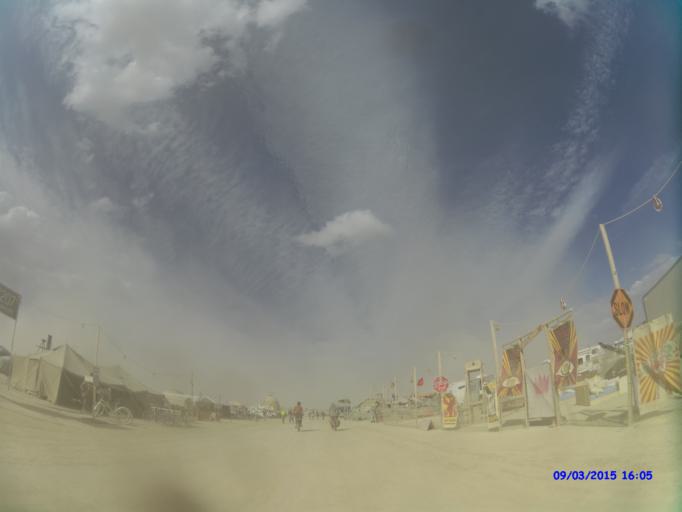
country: US
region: Nevada
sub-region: Pershing County
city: Lovelock
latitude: 40.7808
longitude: -119.1966
